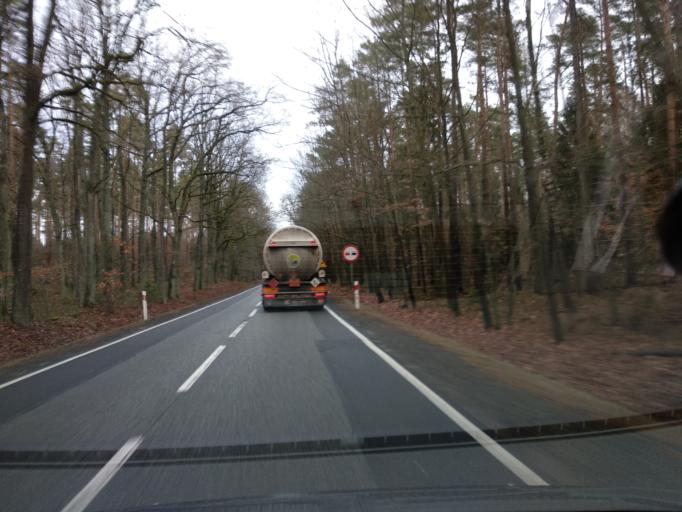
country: PL
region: Lower Silesian Voivodeship
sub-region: Powiat olesnicki
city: Twardogora
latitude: 51.3104
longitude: 17.5470
